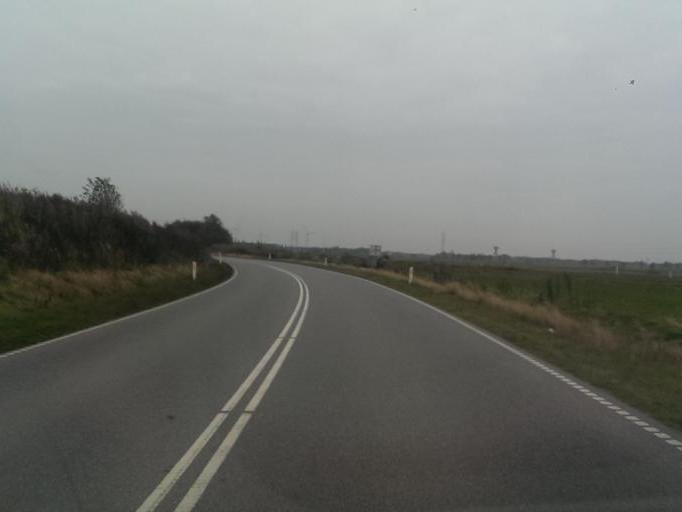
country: DK
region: South Denmark
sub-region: Esbjerg Kommune
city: Tjaereborg
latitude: 55.4637
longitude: 8.5567
